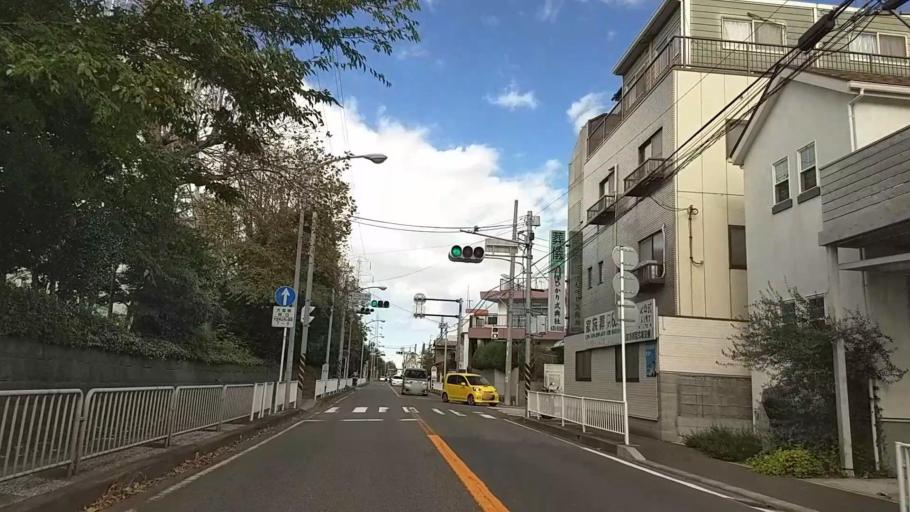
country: JP
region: Kanagawa
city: Yokohama
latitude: 35.4957
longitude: 139.6369
